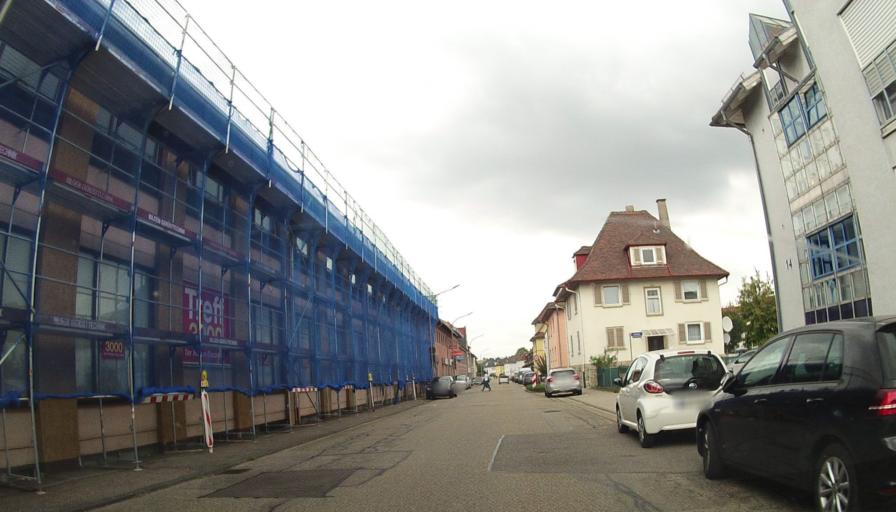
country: DE
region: Baden-Wuerttemberg
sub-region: Karlsruhe Region
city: Gaggenau
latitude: 48.8052
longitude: 8.3225
